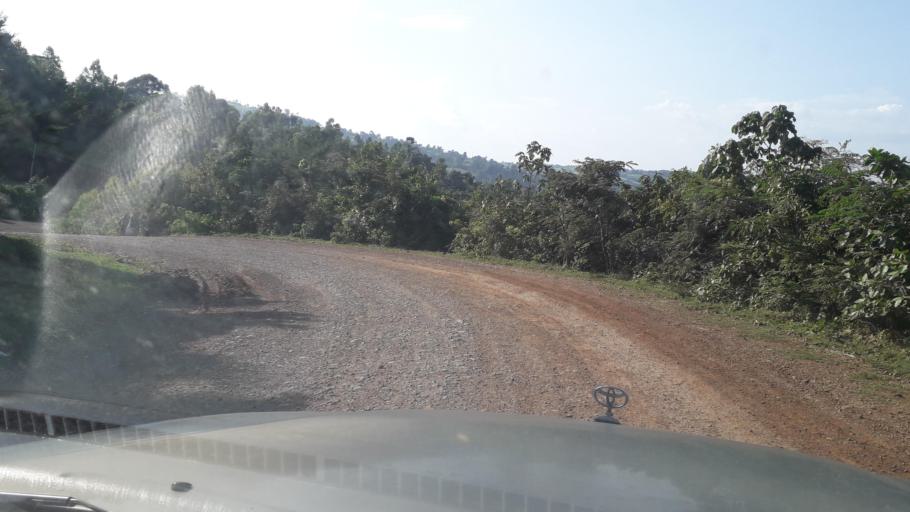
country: ET
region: Oromiya
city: Jima
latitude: 7.4676
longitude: 36.8766
